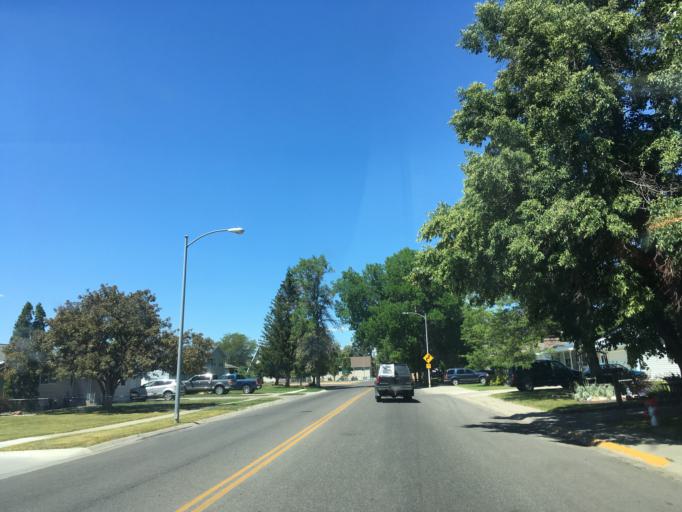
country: US
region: Montana
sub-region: Yellowstone County
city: Billings
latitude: 45.7714
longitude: -108.5647
